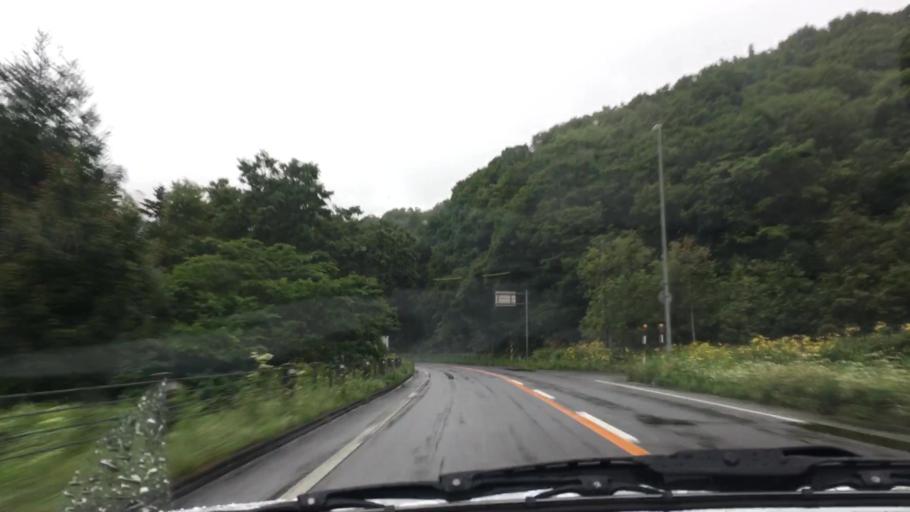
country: JP
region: Hokkaido
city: Niseko Town
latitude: 42.6028
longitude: 140.6181
